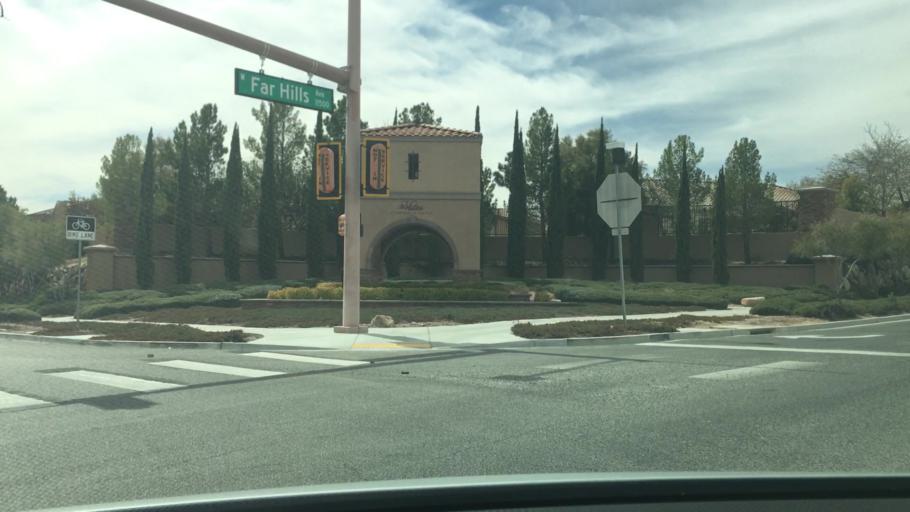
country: US
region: Nevada
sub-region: Clark County
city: Summerlin South
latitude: 36.1805
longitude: -115.3456
